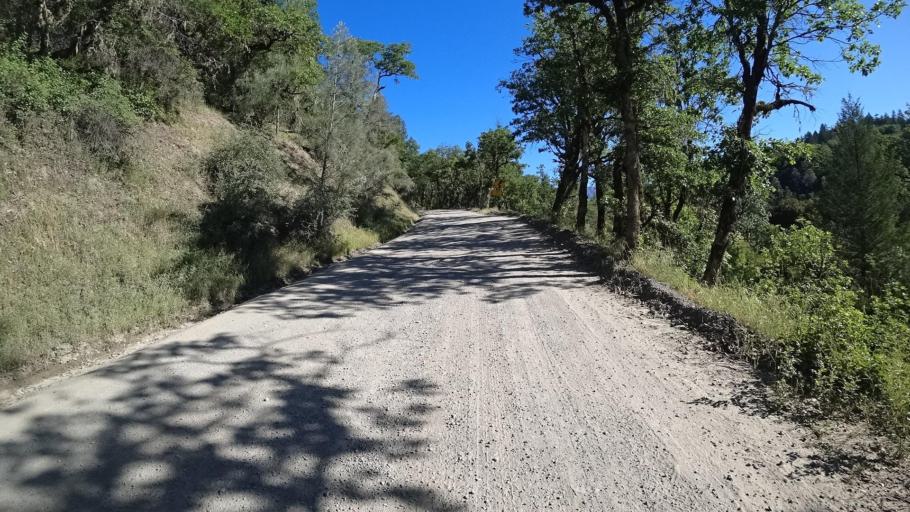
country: US
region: California
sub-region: Lake County
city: Upper Lake
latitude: 39.4202
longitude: -122.9795
